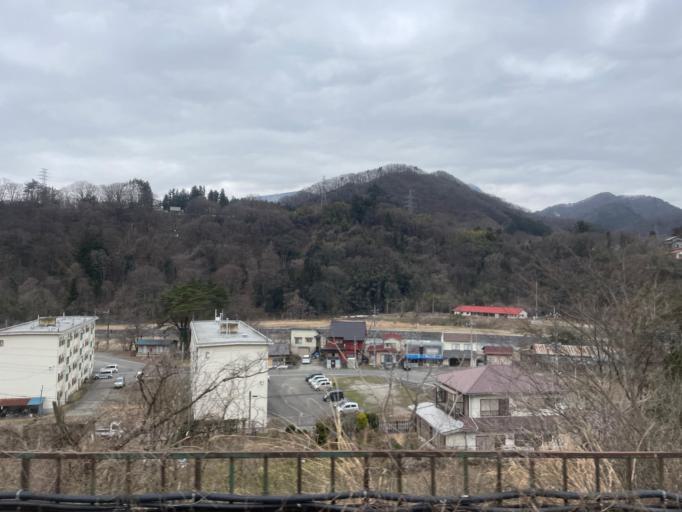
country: JP
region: Gunma
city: Numata
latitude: 36.7520
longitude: 138.9780
